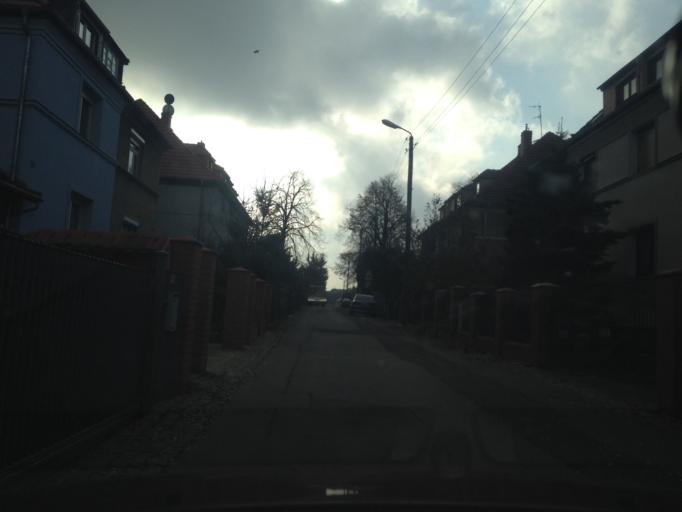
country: PL
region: Lower Silesian Voivodeship
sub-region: Powiat zgorzelecki
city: Zgorzelec
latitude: 51.1554
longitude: 15.0103
